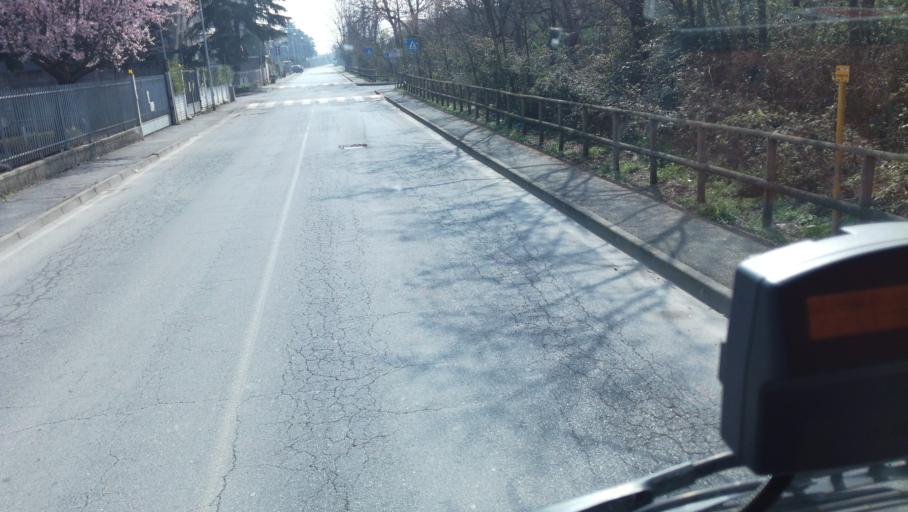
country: IT
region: Lombardy
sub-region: Citta metropolitana di Milano
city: Fizzonasco
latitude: 45.3737
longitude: 9.1806
